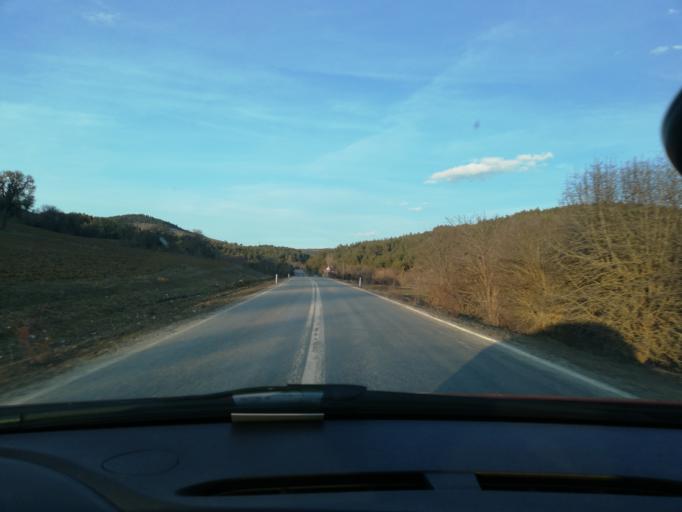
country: TR
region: Kastamonu
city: Agli
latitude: 41.6963
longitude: 33.6301
